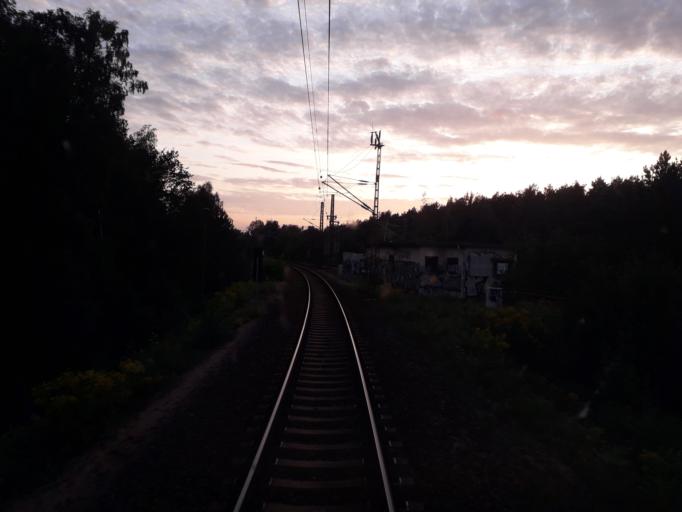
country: DE
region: Brandenburg
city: Hennigsdorf
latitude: 52.6587
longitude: 13.1963
